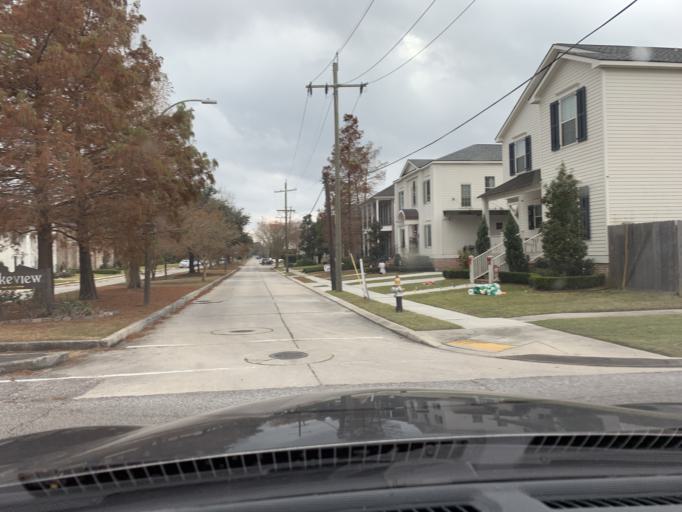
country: US
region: Louisiana
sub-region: Jefferson Parish
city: Metairie
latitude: 30.0191
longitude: -90.1011
